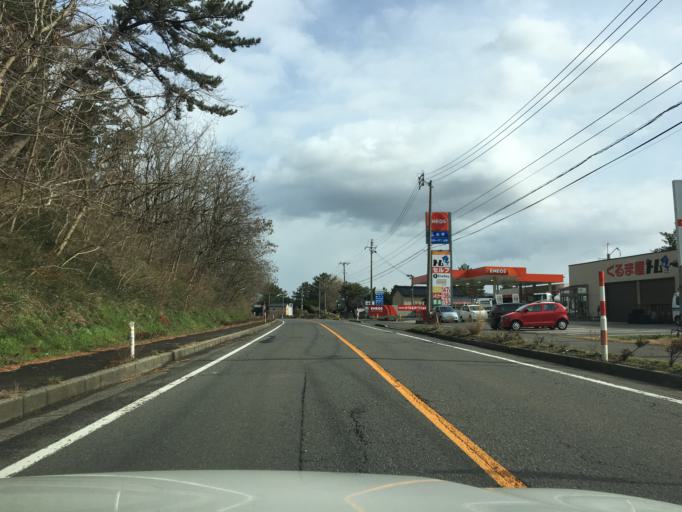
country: JP
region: Yamagata
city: Yuza
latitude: 39.2332
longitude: 139.9092
